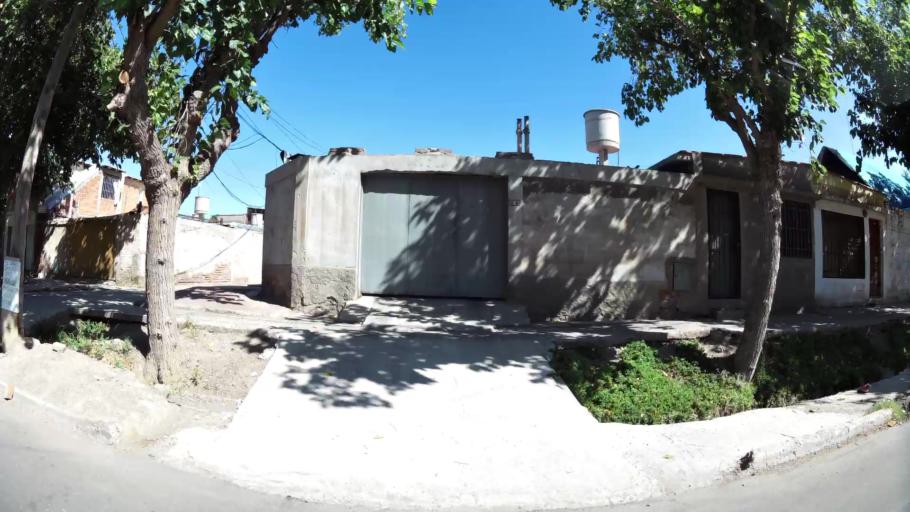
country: AR
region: Mendoza
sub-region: Departamento de Godoy Cruz
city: Godoy Cruz
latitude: -32.9571
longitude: -68.8306
